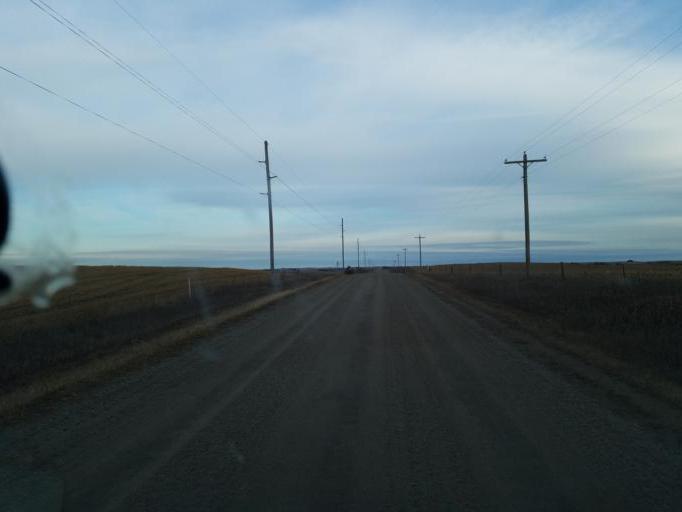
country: US
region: Nebraska
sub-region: Knox County
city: Bloomfield
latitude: 42.5730
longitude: -97.6228
